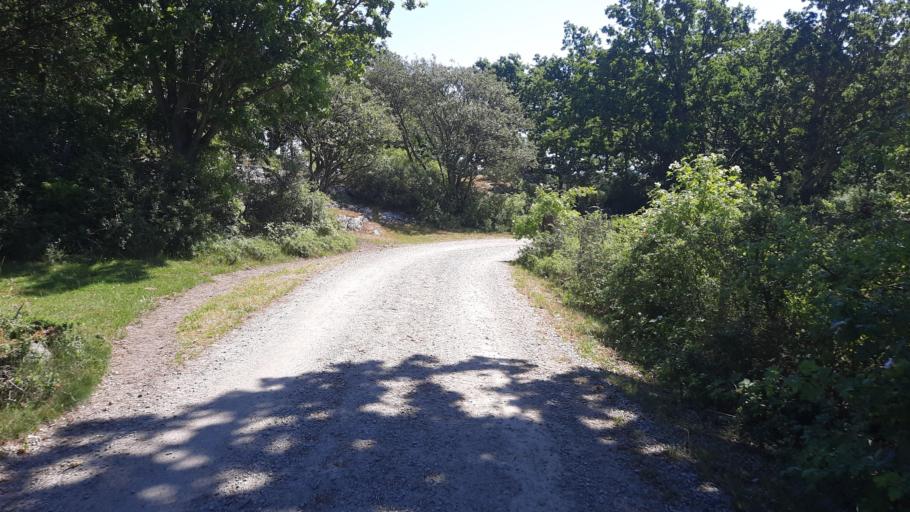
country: SE
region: Blekinge
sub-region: Karlskrona Kommun
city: Jaemjoe
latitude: 56.1532
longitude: 15.7524
